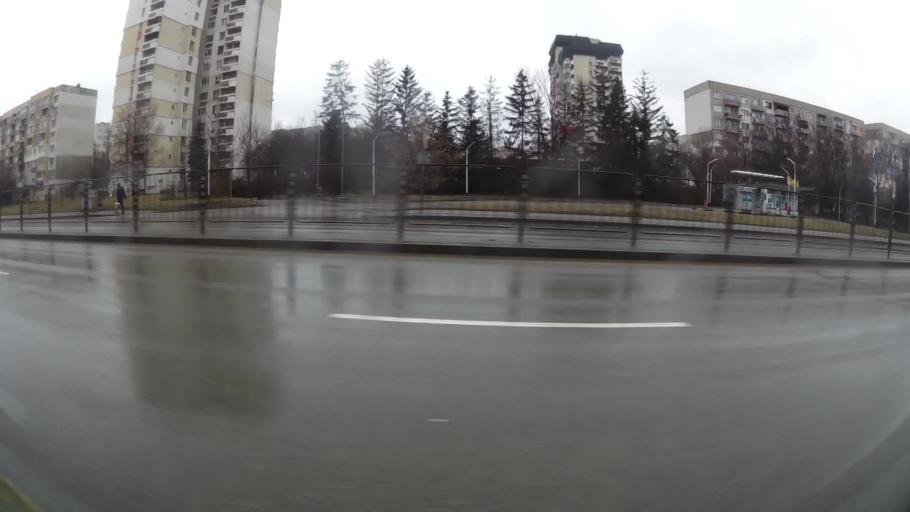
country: BG
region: Sofia-Capital
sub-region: Stolichna Obshtina
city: Sofia
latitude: 42.6434
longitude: 23.3734
